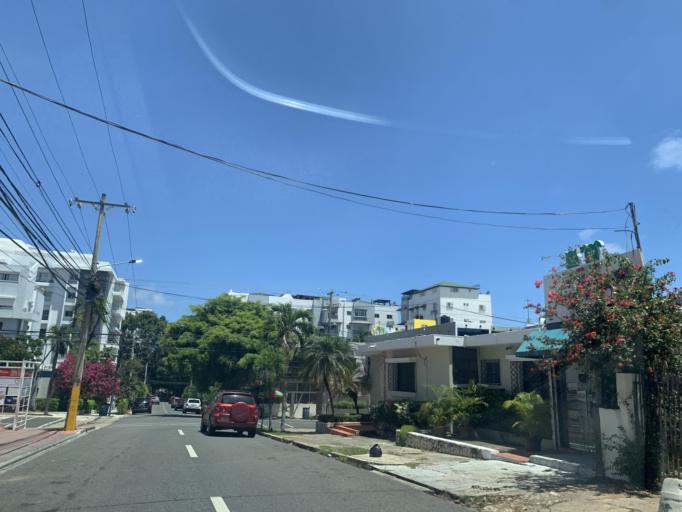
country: DO
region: Nacional
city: Ciudad Nueva
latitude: 18.4664
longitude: -69.9068
